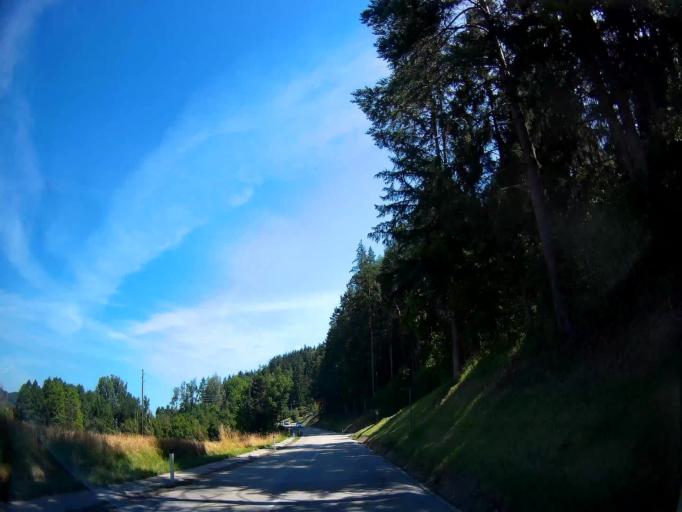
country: AT
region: Carinthia
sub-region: Politischer Bezirk Sankt Veit an der Glan
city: St. Georgen am Laengsee
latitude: 46.7685
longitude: 14.4223
